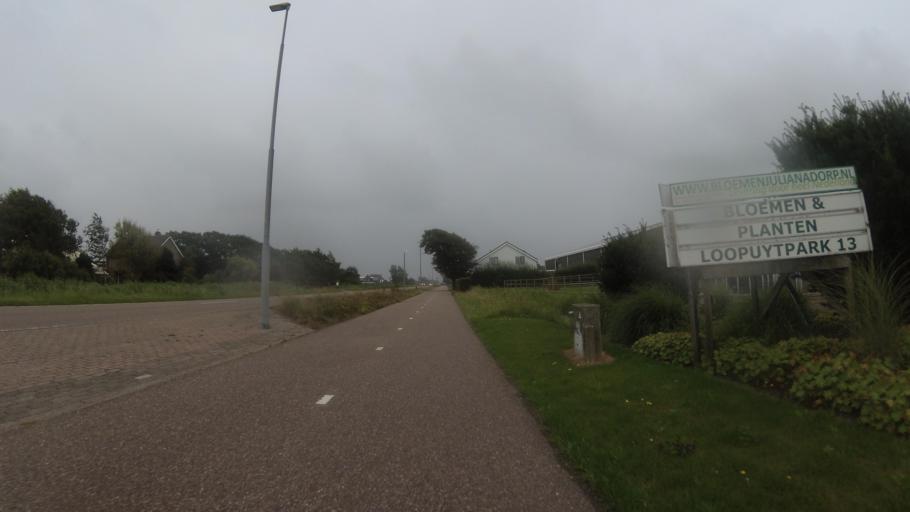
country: NL
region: North Holland
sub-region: Gemeente Den Helder
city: Den Helder
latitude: 52.9090
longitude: 4.7531
